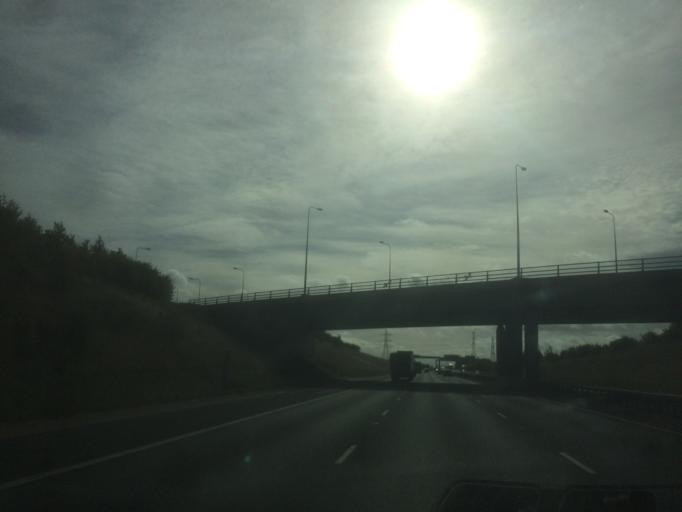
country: GB
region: England
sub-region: City and Borough of Leeds
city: Ledsham
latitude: 53.7641
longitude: -1.2830
